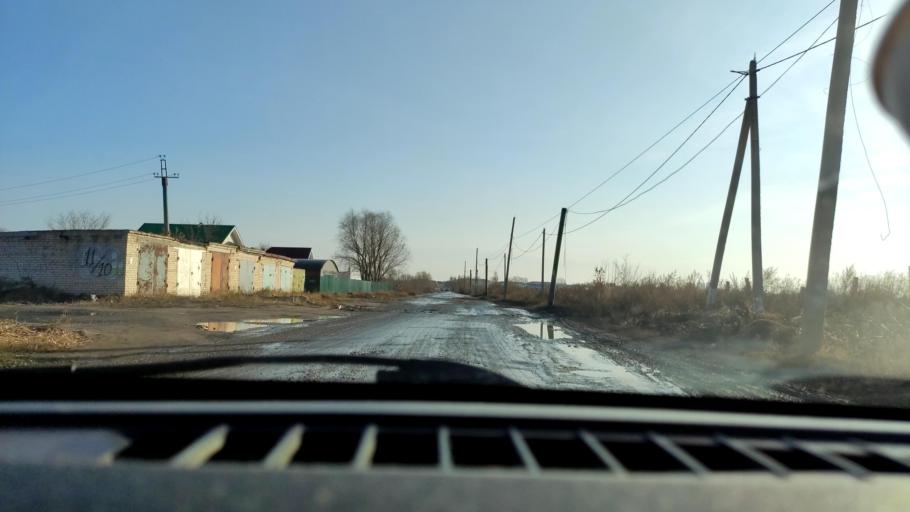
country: RU
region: Samara
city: Samara
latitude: 53.1191
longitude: 50.1026
